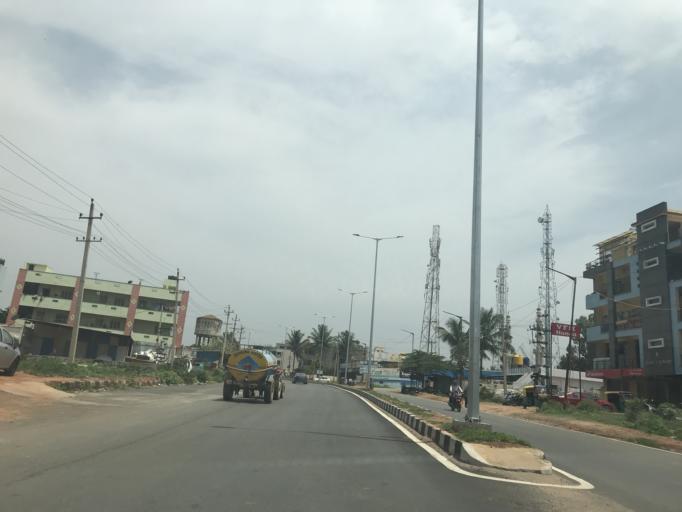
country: IN
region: Karnataka
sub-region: Bangalore Urban
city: Yelahanka
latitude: 13.1317
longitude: 77.6668
